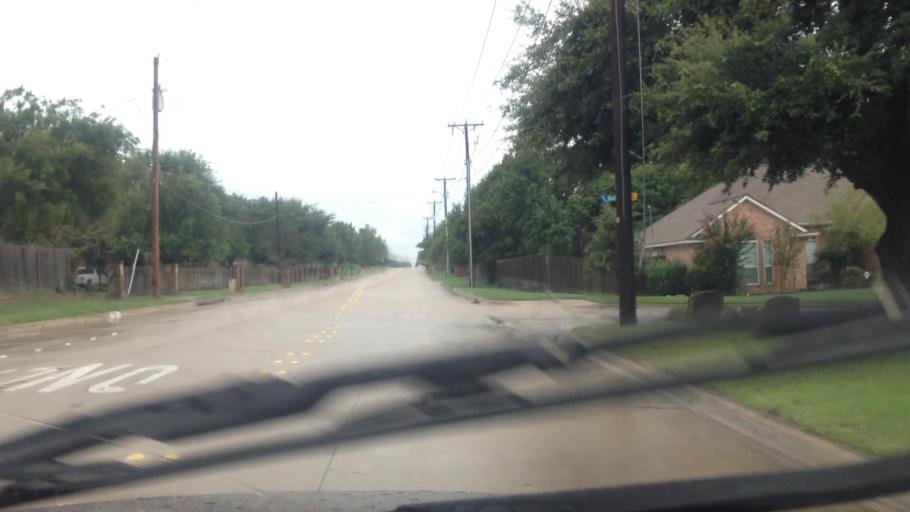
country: US
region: Texas
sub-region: Tarrant County
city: Watauga
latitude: 32.8922
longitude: -97.2291
